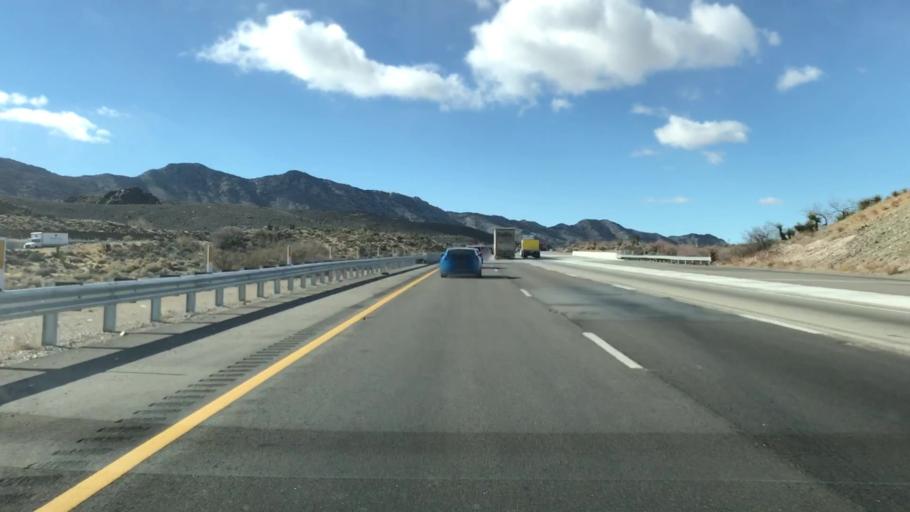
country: US
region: Nevada
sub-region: Clark County
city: Sandy Valley
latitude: 35.4689
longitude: -115.5158
